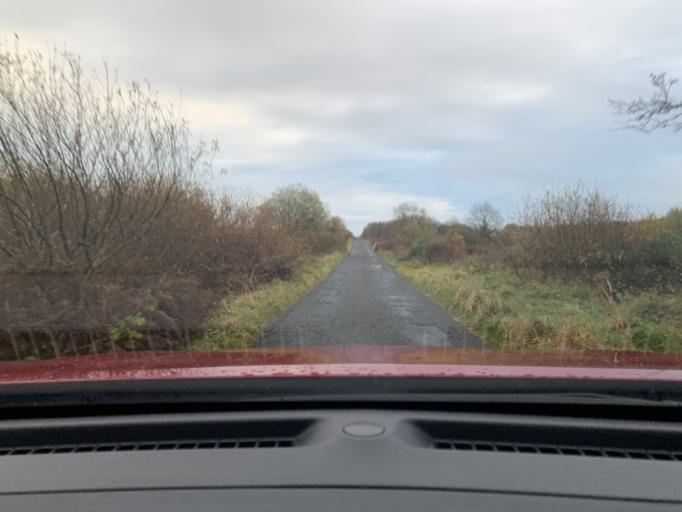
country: IE
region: Connaught
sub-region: Sligo
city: Ballymote
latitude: 54.0165
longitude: -8.5122
